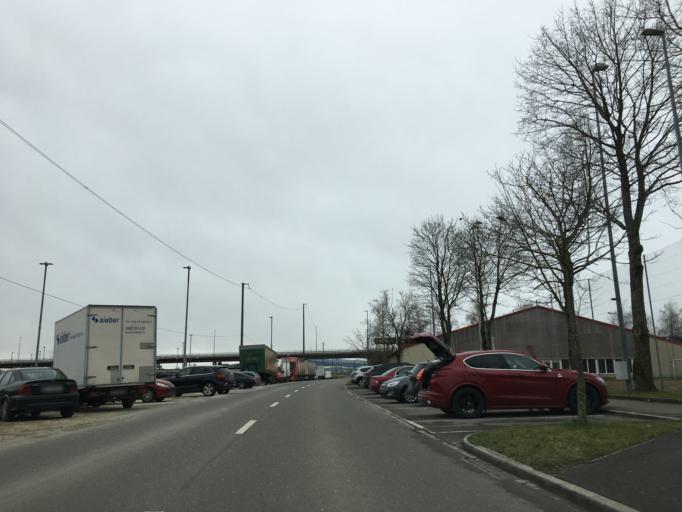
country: CH
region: Aargau
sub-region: Bezirk Baden
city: Spreitenbach
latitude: 47.4243
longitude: 8.3738
